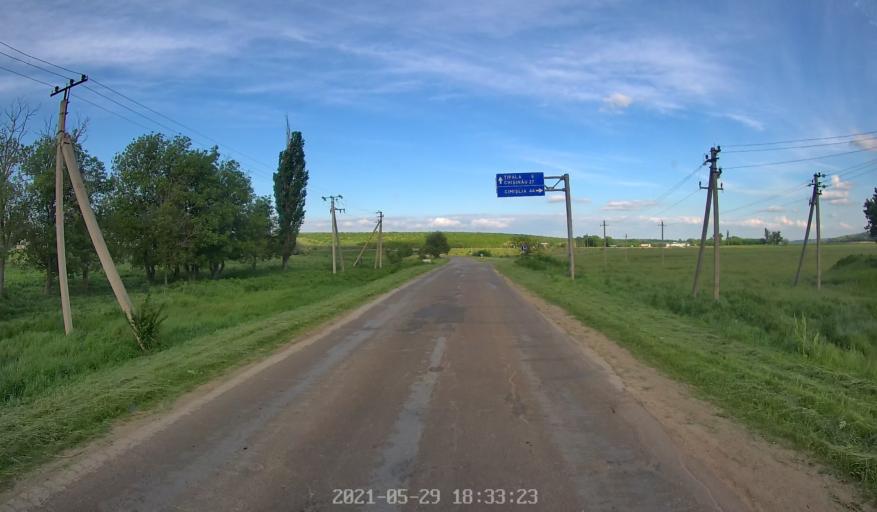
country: MD
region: Chisinau
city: Singera
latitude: 46.8161
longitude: 28.9028
